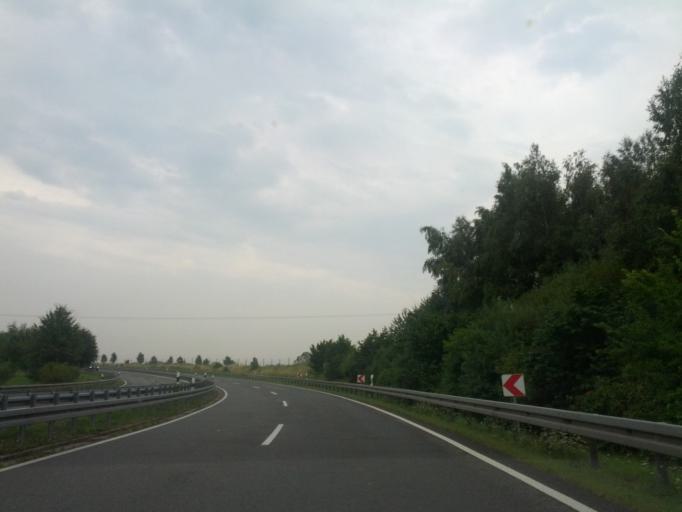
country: DE
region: Mecklenburg-Vorpommern
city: Ziesendorf
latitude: 54.0166
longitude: 12.0614
